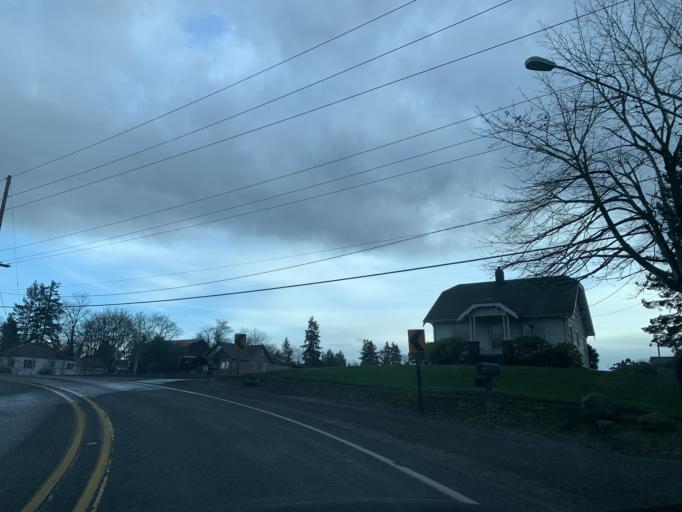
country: US
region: Washington
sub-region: Pierce County
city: Milton
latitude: 47.2357
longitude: -122.3074
